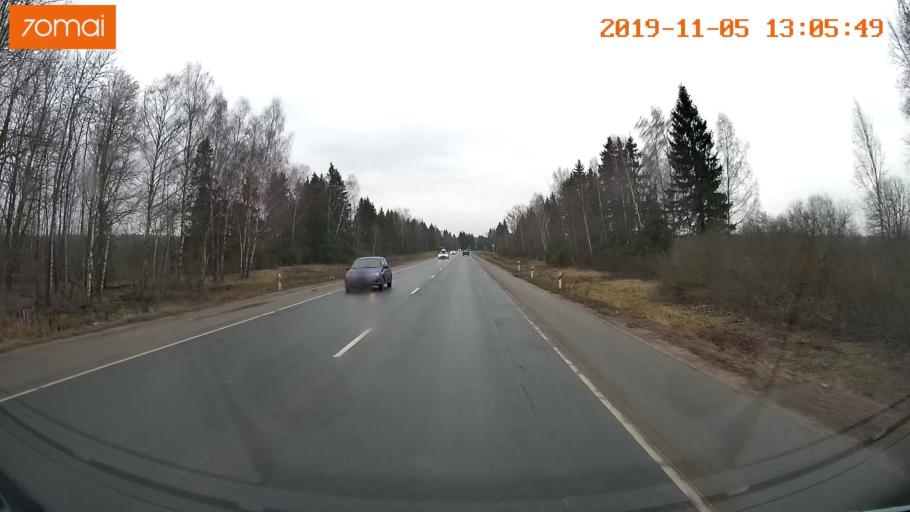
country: RU
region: Ivanovo
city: Kitovo
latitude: 56.8801
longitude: 41.2512
